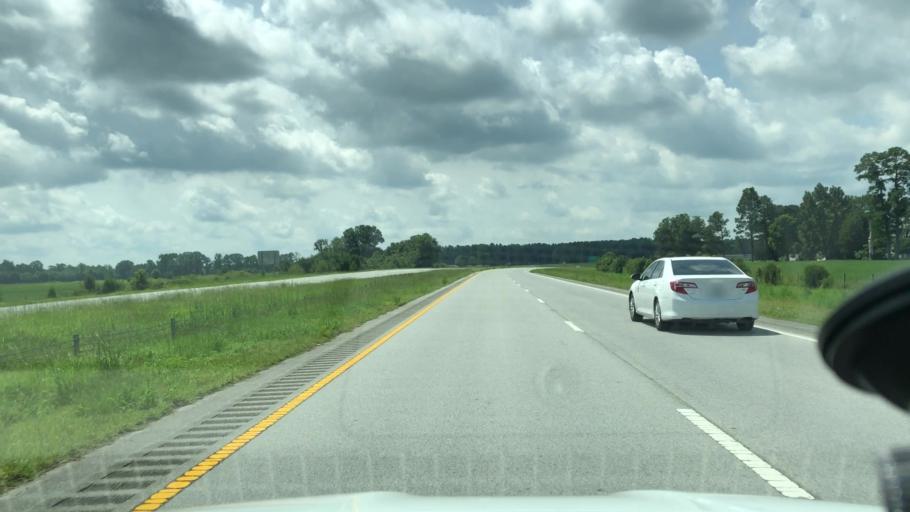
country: US
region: North Carolina
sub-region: Beaufort County
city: Washington
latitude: 35.5131
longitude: -77.0866
